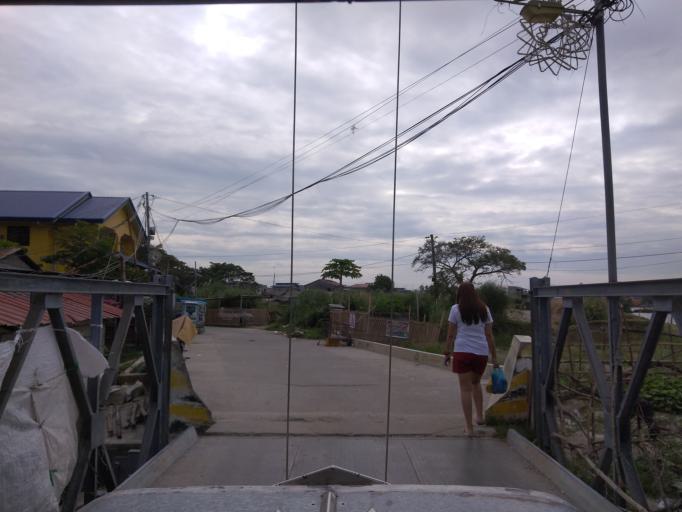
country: PH
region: Central Luzon
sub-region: Province of Pampanga
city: Sexmoan
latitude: 14.9321
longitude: 120.6263
